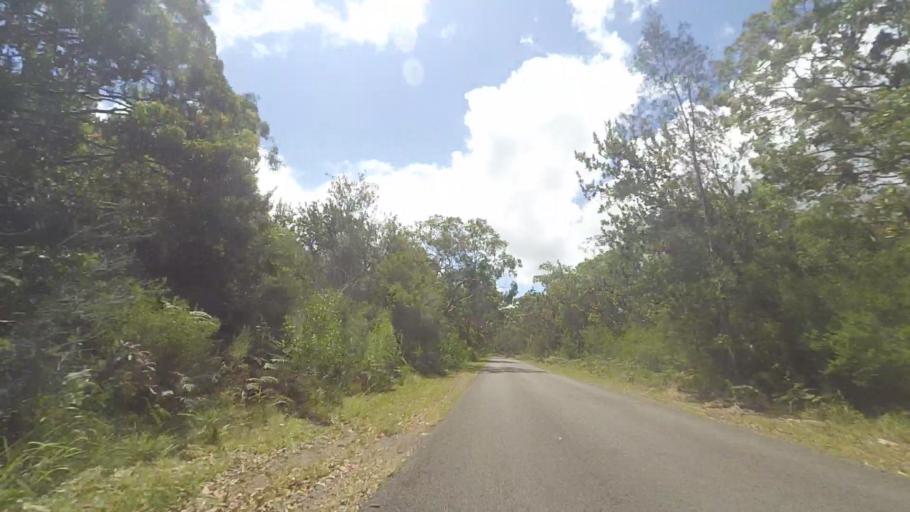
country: AU
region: New South Wales
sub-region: Great Lakes
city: Bulahdelah
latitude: -32.5119
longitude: 152.3203
